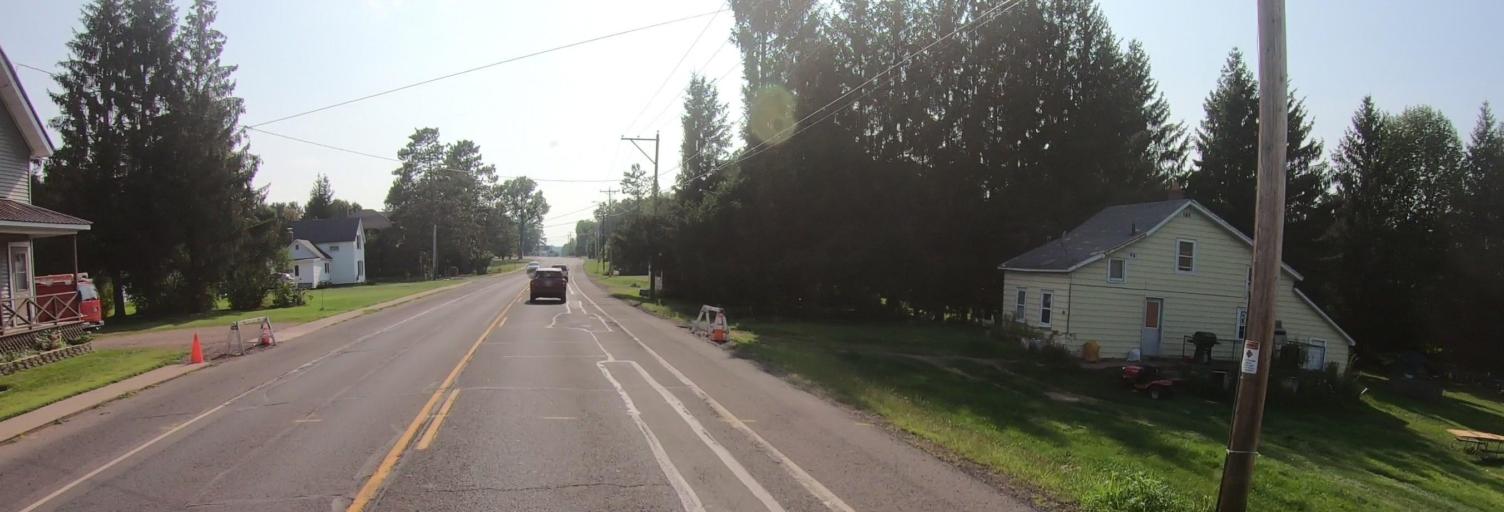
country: US
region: Wisconsin
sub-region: Iron County
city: Hurley
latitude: 46.4391
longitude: -90.2110
